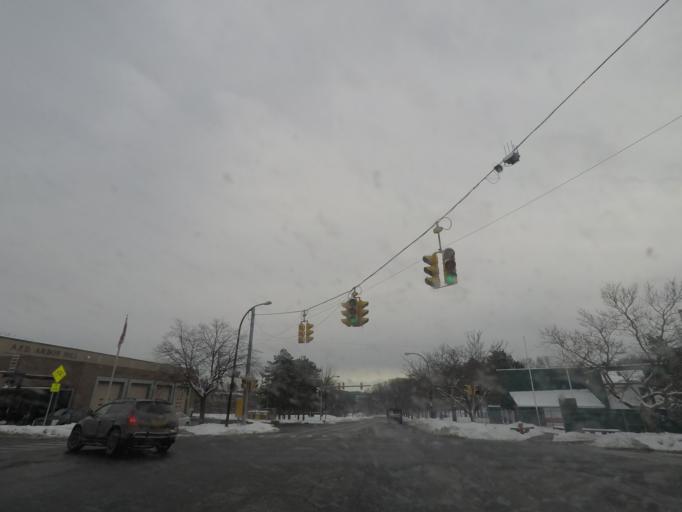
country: US
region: New York
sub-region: Albany County
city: Albany
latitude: 42.6647
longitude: -73.7541
